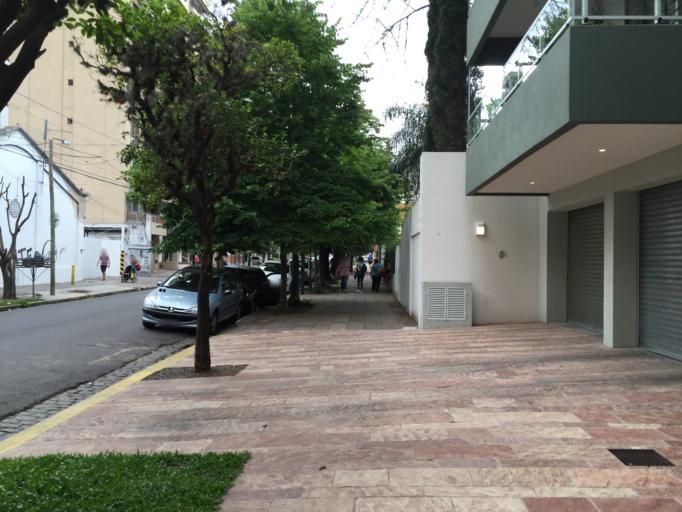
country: AR
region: Buenos Aires
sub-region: Partido de Lomas de Zamora
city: Lomas de Zamora
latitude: -34.7571
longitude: -58.3993
